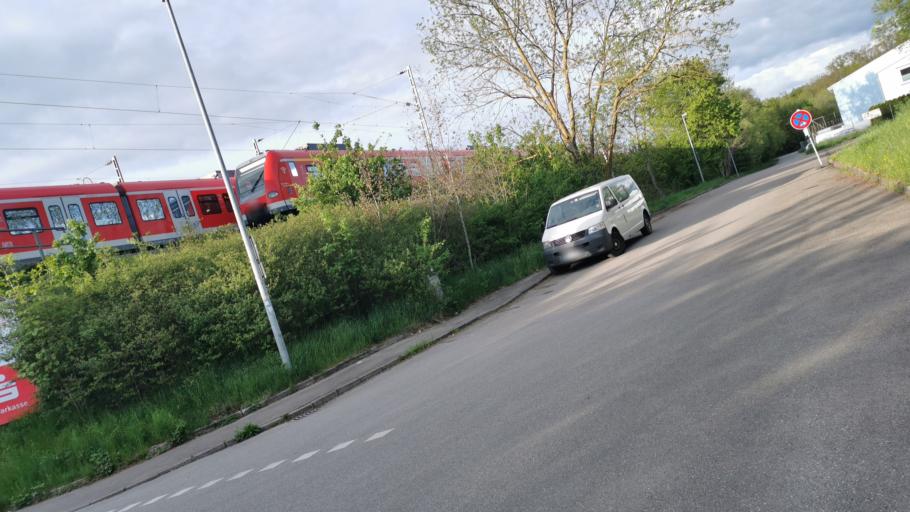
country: DE
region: Baden-Wuerttemberg
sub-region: Regierungsbezirk Stuttgart
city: Korntal
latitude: 48.8300
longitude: 9.1346
